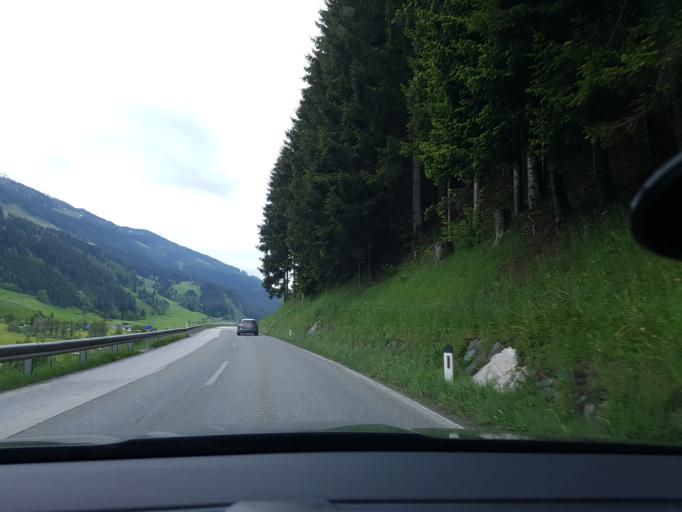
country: AT
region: Tyrol
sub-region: Politischer Bezirk Kitzbuhel
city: Jochberg
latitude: 47.3680
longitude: 12.4161
